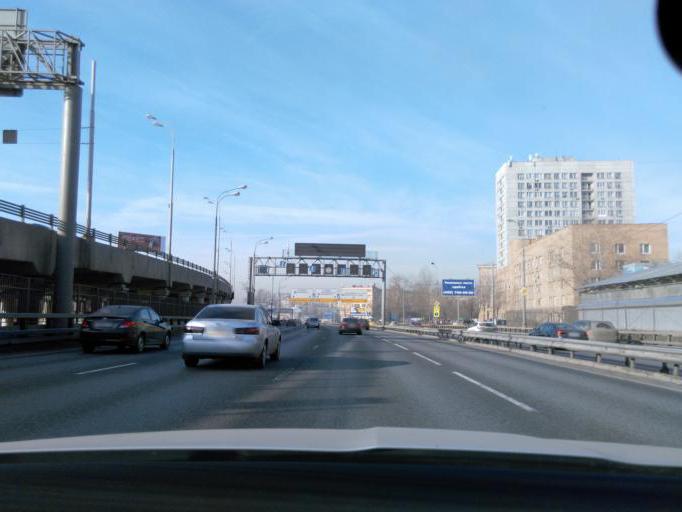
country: RU
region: Moskovskaya
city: Kozhukhovo
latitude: 55.7122
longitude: 37.6742
